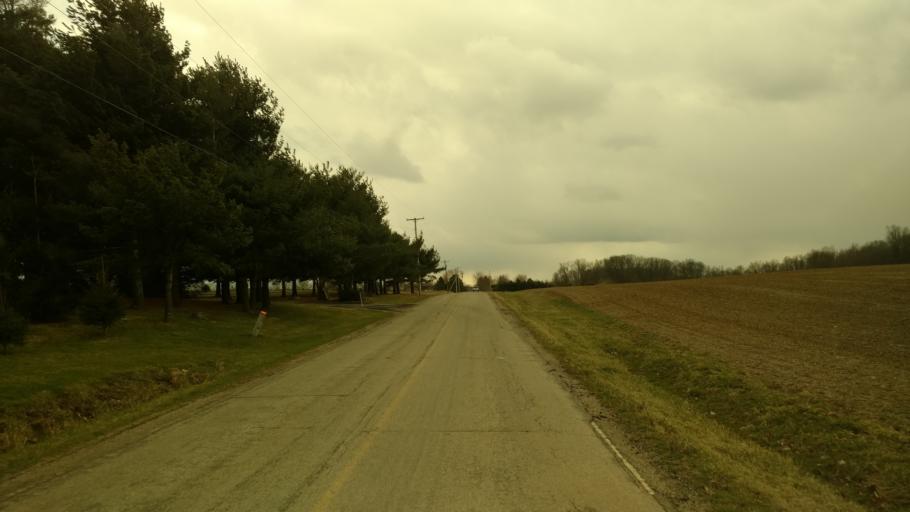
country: US
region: Ohio
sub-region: Crawford County
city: Crestline
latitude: 40.7530
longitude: -82.6982
